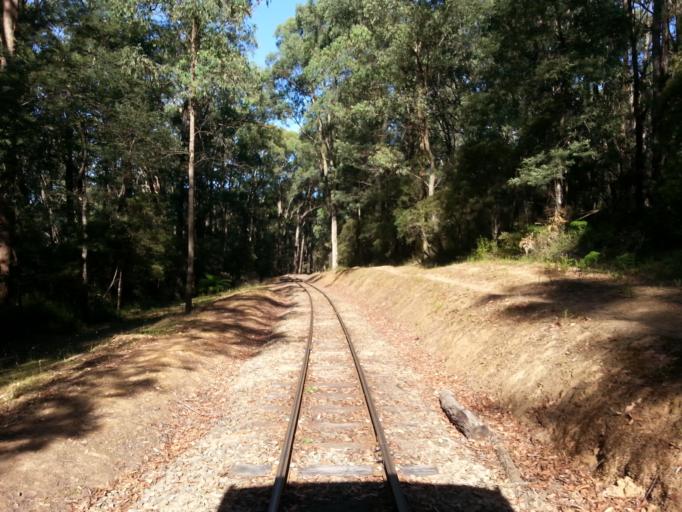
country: AU
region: Victoria
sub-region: Cardinia
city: Cockatoo
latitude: -37.9293
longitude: 145.4740
